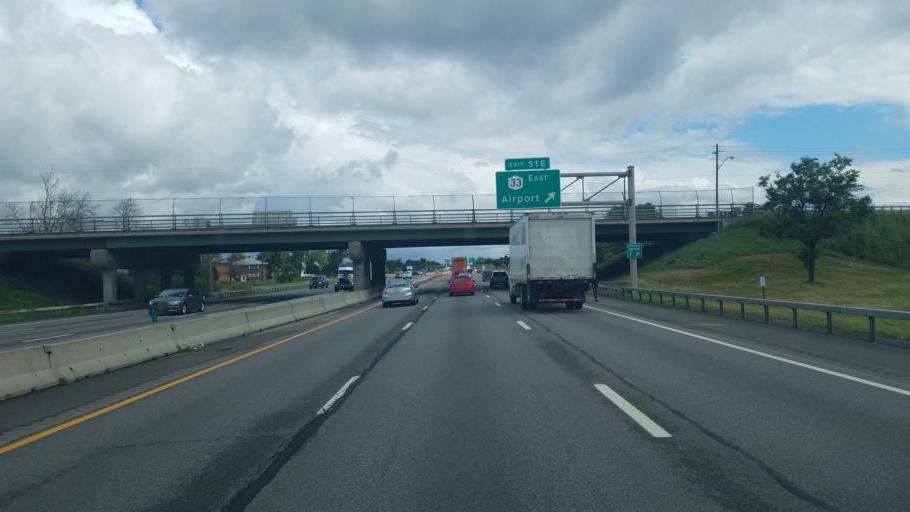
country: US
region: New York
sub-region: Erie County
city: Cheektowaga
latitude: 42.9242
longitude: -78.7661
